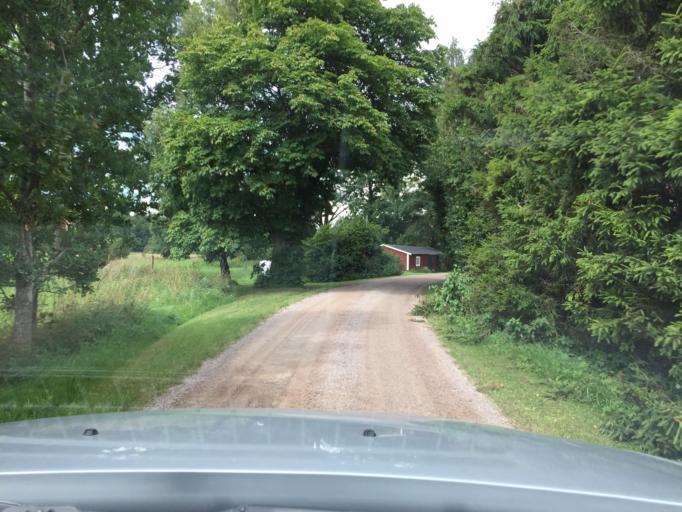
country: SE
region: Skane
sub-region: Hassleholms Kommun
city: Sosdala
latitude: 56.0161
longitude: 13.6493
